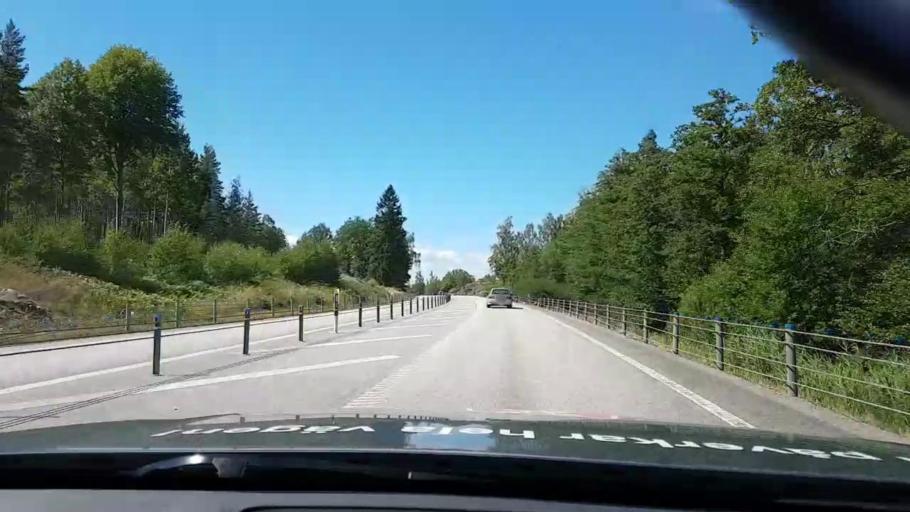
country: SE
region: Kalmar
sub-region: Vasterviks Kommun
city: Gamleby
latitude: 57.8610
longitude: 16.4265
